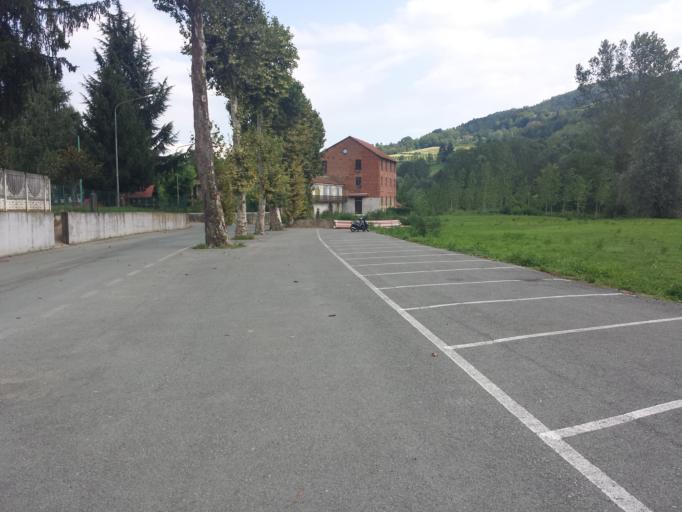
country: IT
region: Piedmont
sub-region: Provincia di Asti
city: Monastero Bormida
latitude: 44.6462
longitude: 8.3260
